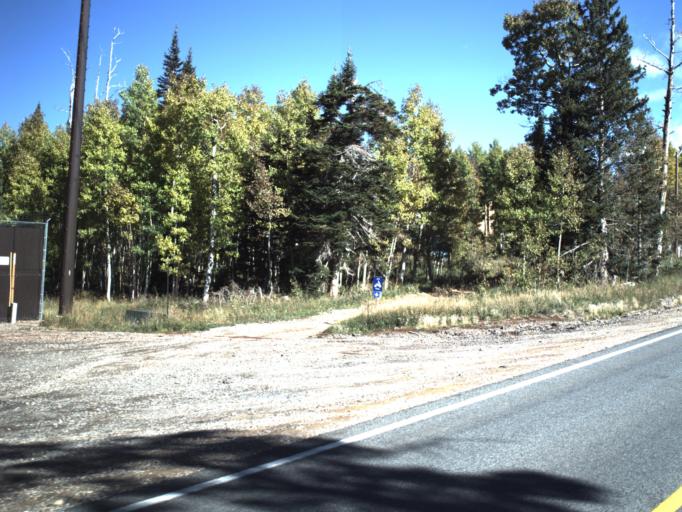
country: US
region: Utah
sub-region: Iron County
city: Parowan
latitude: 37.7064
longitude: -112.8503
